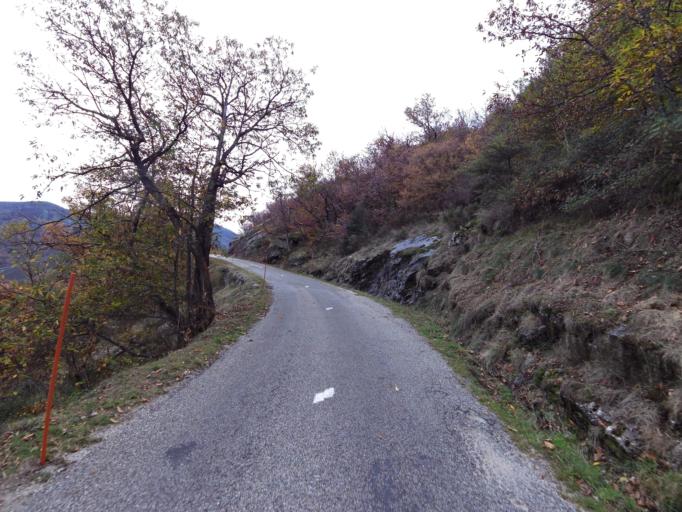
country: FR
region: Rhone-Alpes
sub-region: Departement de l'Ardeche
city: Les Vans
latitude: 44.5257
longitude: 4.0483
